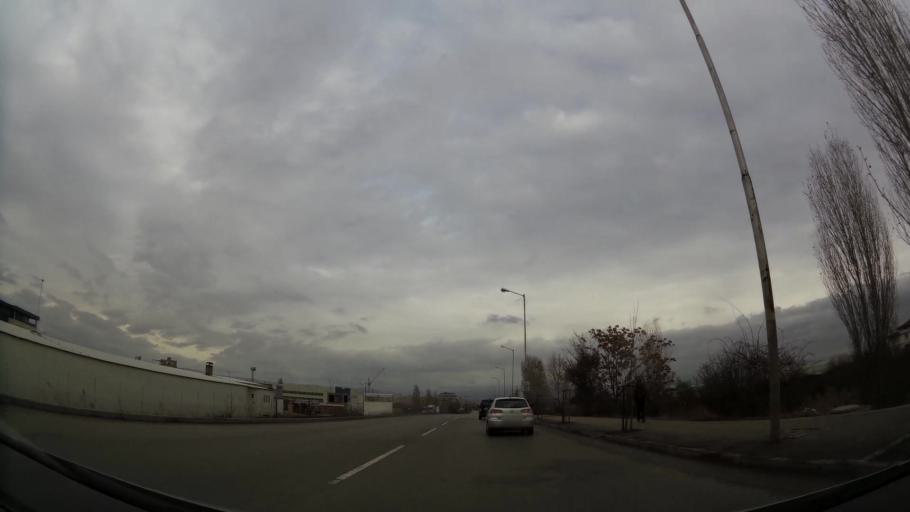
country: BG
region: Sofiya
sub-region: Obshtina Bozhurishte
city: Bozhurishte
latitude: 42.7287
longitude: 23.2638
